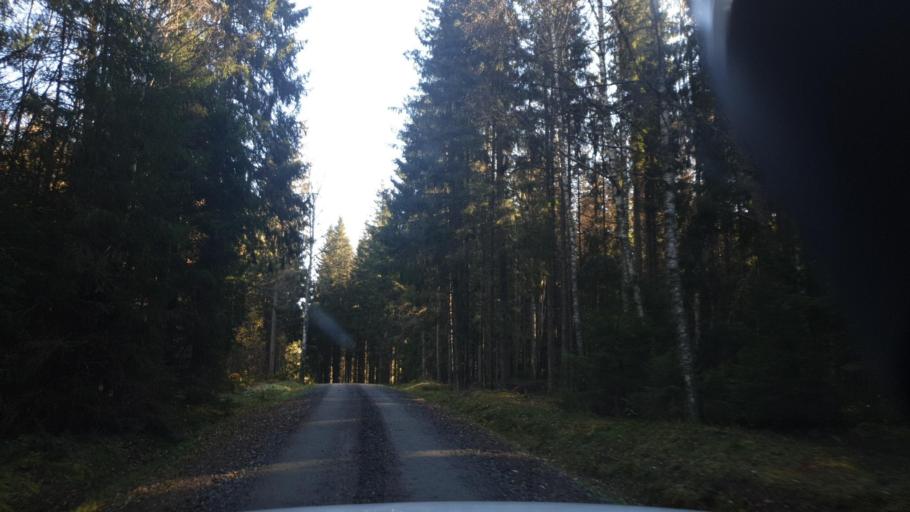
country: SE
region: Vaermland
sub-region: Karlstads Kommun
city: Edsvalla
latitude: 59.4621
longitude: 13.1046
